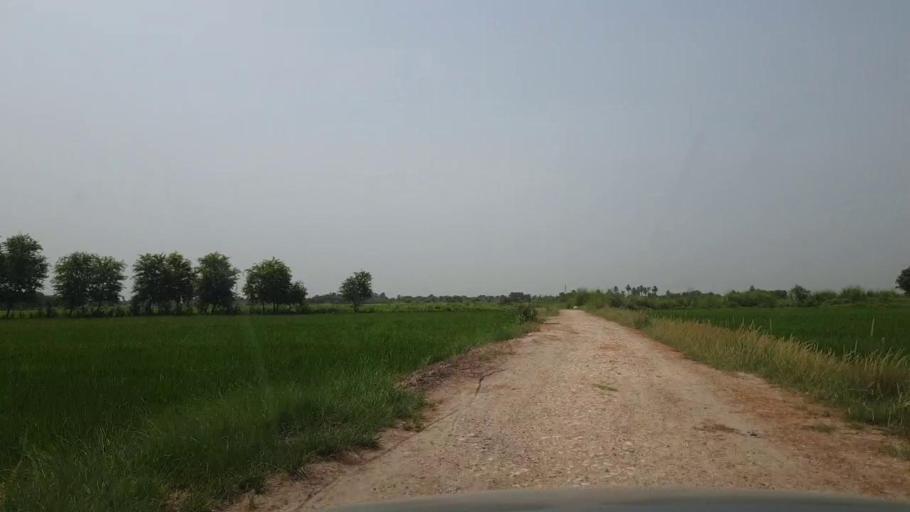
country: PK
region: Sindh
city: Madeji
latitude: 27.7936
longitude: 68.5378
